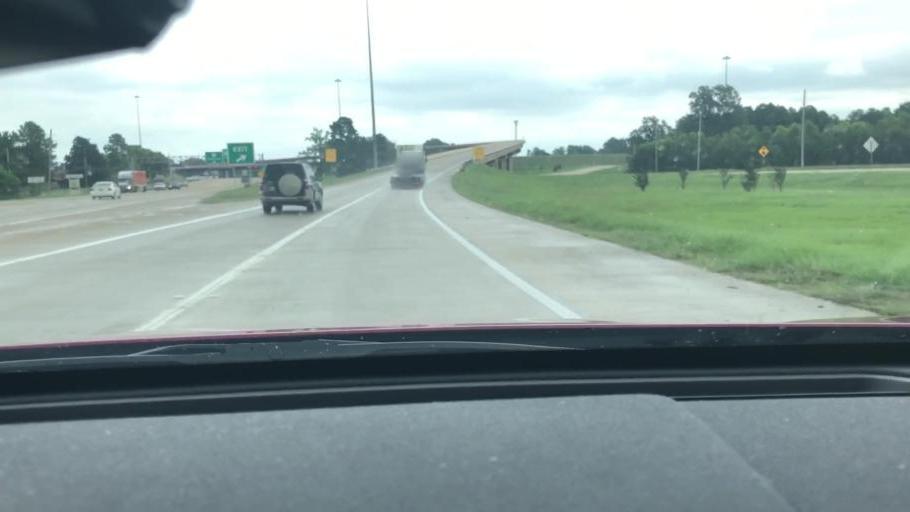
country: US
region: Texas
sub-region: Bowie County
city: Wake Village
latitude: 33.3917
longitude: -94.1029
